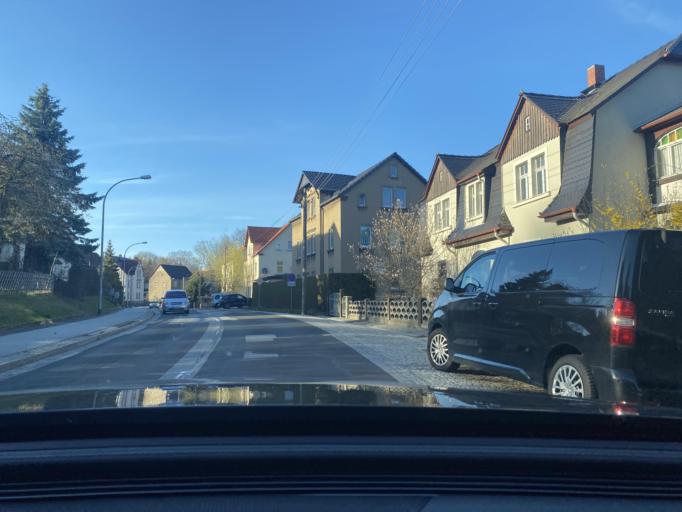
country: DE
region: Saxony
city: Schirgiswalde
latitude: 51.0844
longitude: 14.4259
